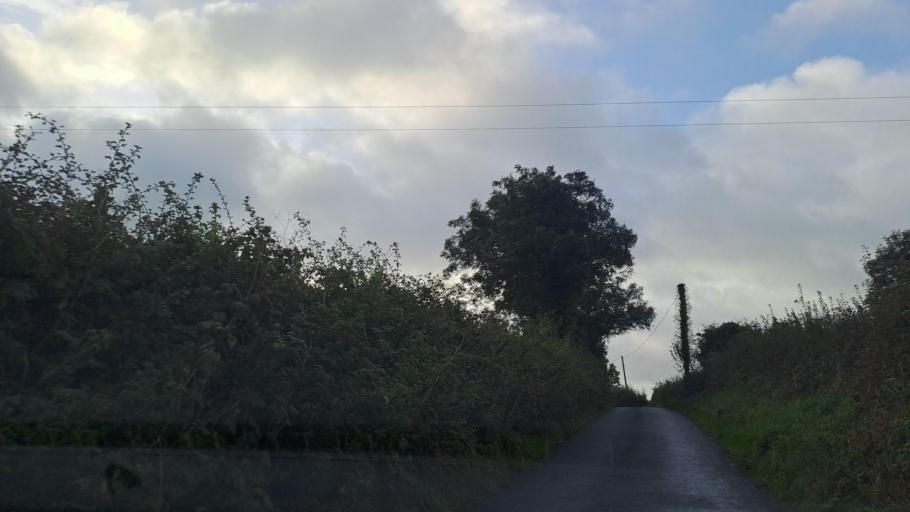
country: IE
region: Ulster
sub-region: An Cabhan
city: Kingscourt
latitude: 53.9688
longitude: -6.8426
